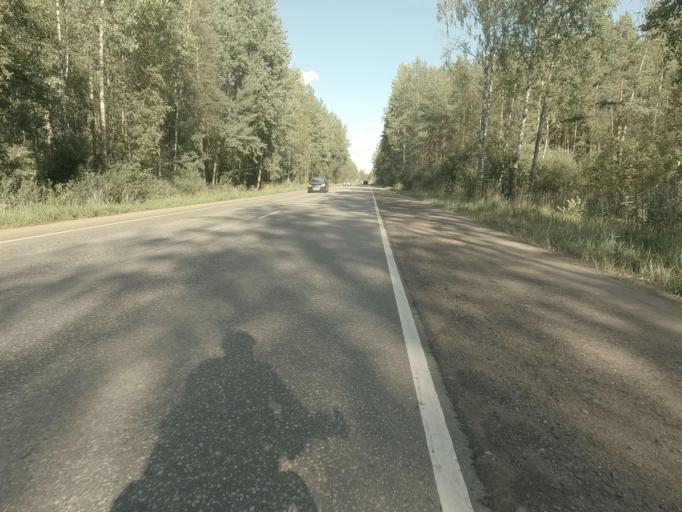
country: RU
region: Leningrad
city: Imeni Morozova
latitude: 59.9739
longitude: 30.9991
